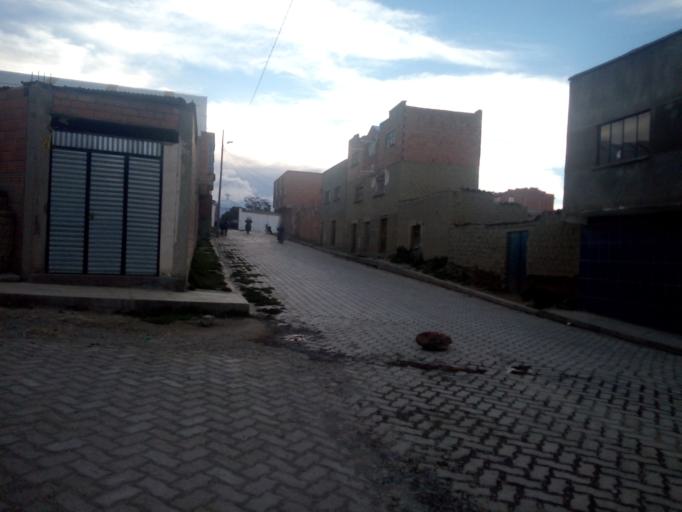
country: BO
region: La Paz
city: Achacachi
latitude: -16.0453
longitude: -68.6887
